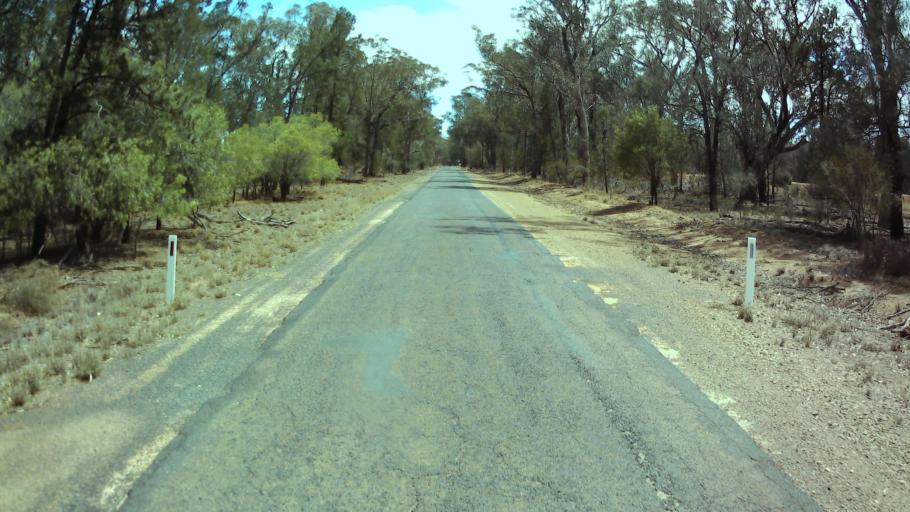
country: AU
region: New South Wales
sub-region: Weddin
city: Grenfell
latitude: -33.6474
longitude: 148.1926
